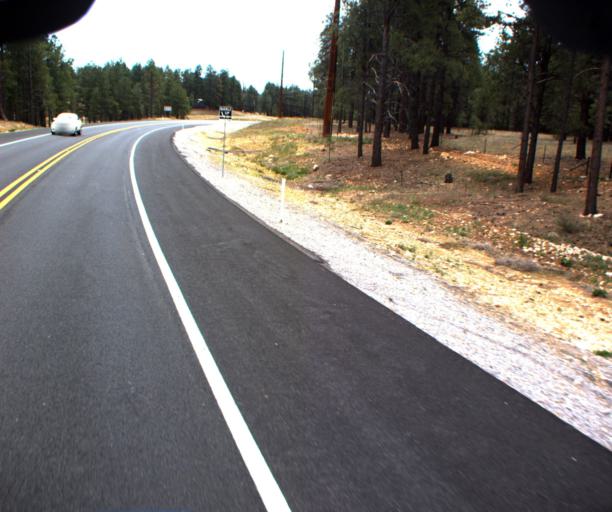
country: US
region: Arizona
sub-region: Coconino County
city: Kachina Village
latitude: 35.1373
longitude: -111.6864
